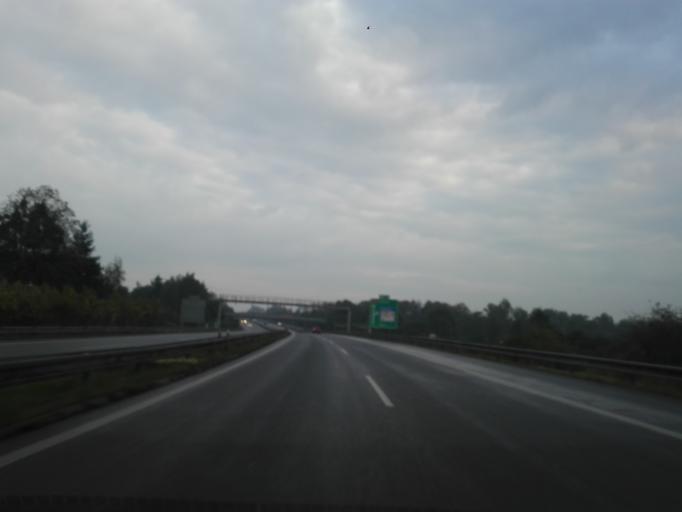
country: CZ
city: Paskov
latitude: 49.7345
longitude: 18.2822
